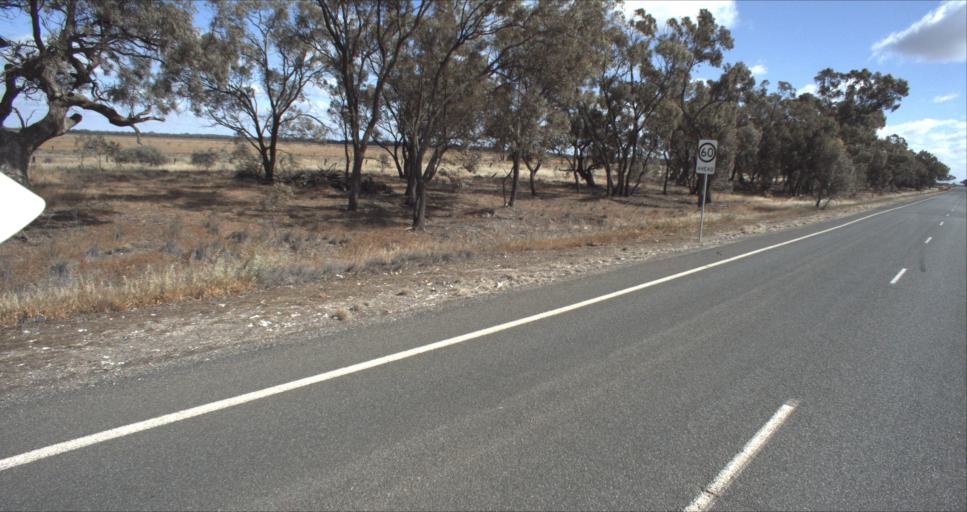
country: AU
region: New South Wales
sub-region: Murrumbidgee Shire
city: Darlington Point
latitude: -34.5580
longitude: 146.1695
